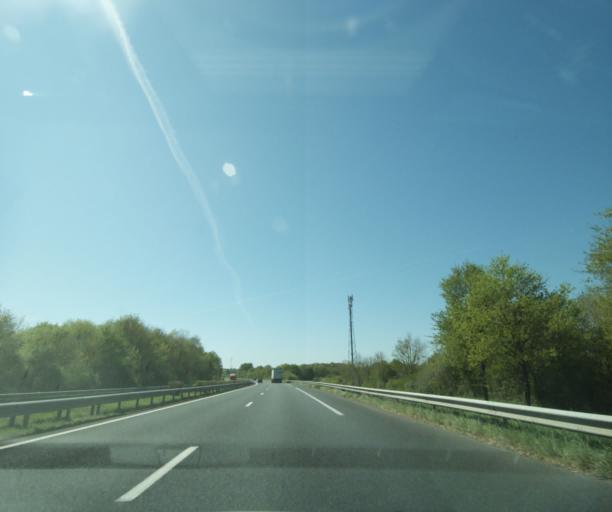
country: FR
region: Centre
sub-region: Departement de l'Indre
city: Luant
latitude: 46.7063
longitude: 1.5870
